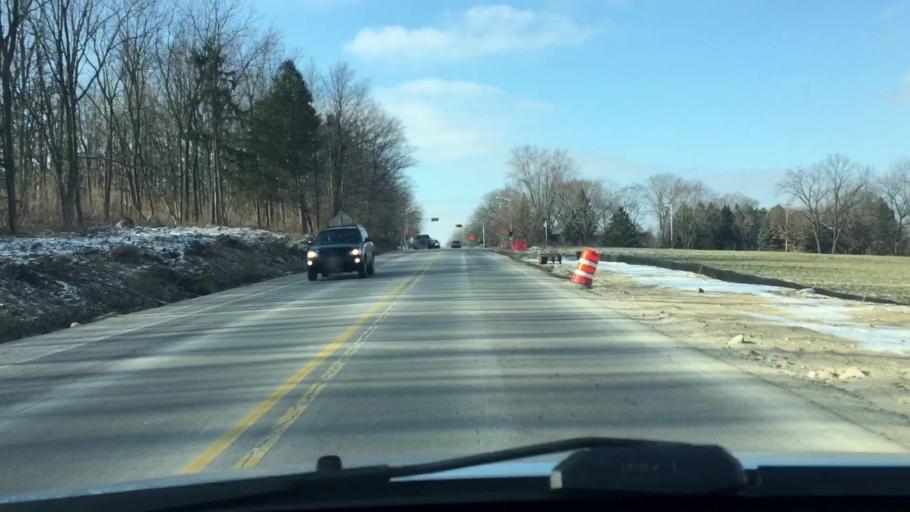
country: US
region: Wisconsin
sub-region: Waukesha County
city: Waukesha
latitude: 42.9886
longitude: -88.2867
